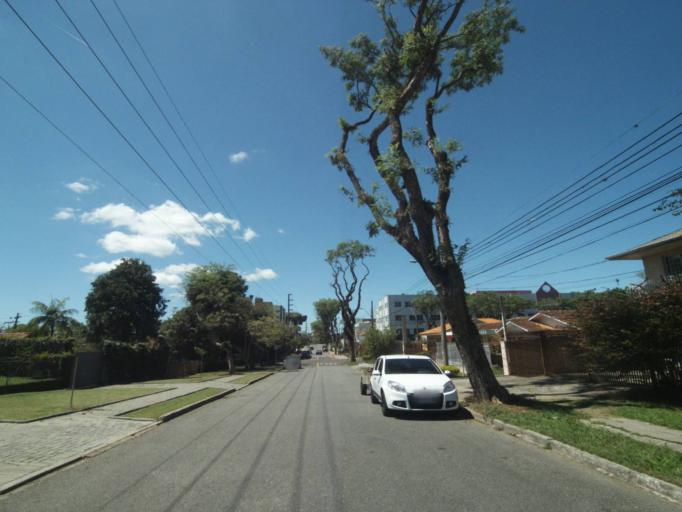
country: BR
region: Parana
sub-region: Curitiba
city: Curitiba
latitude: -25.3925
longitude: -49.2439
